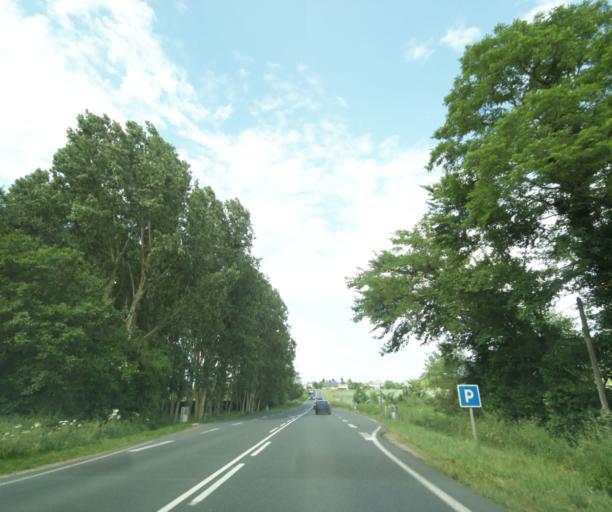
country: FR
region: Pays de la Loire
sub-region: Departement de Maine-et-Loire
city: Distre
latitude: 47.1906
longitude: -0.1281
